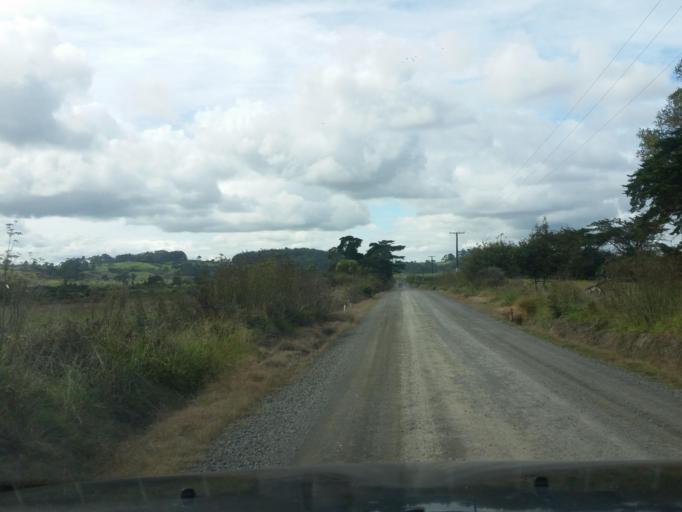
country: NZ
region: Northland
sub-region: Kaipara District
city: Dargaville
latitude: -35.9065
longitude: 173.8036
